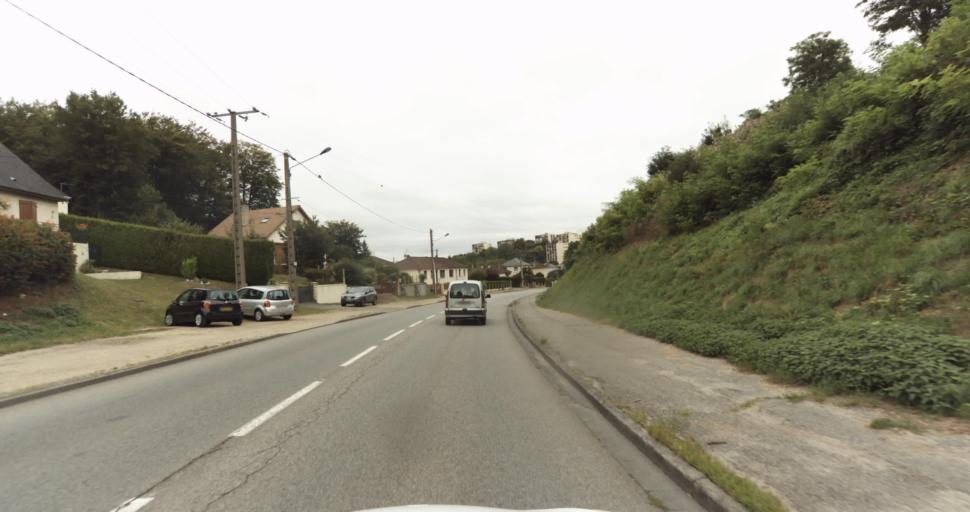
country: FR
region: Haute-Normandie
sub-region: Departement de l'Eure
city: Evreux
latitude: 49.0259
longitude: 1.1665
